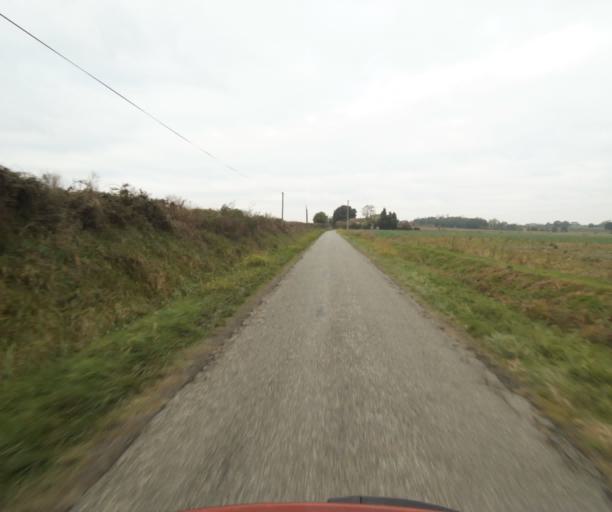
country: FR
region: Midi-Pyrenees
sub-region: Departement du Tarn-et-Garonne
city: Verdun-sur-Garonne
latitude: 43.8118
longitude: 1.2086
